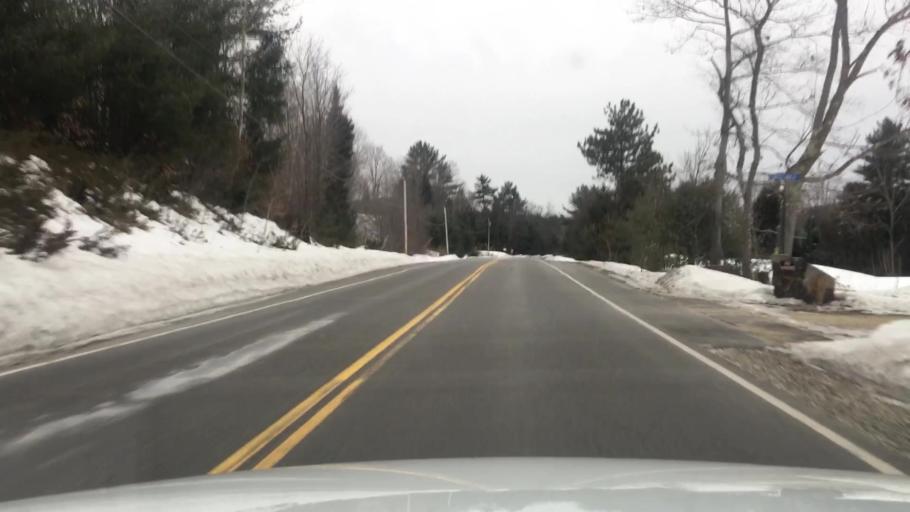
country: US
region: Maine
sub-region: York County
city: Limerick
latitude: 43.7164
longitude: -70.8139
